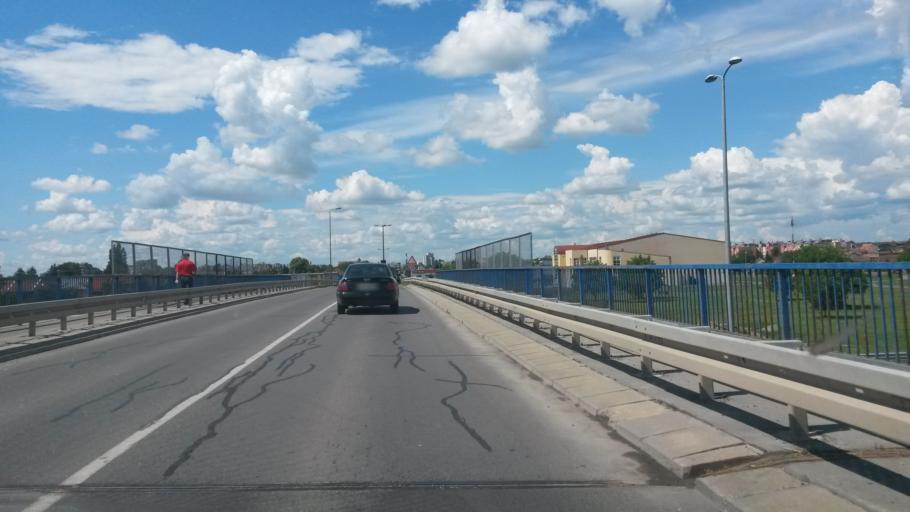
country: HR
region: Osjecko-Baranjska
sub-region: Grad Osijek
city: Osijek
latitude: 45.5406
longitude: 18.7098
